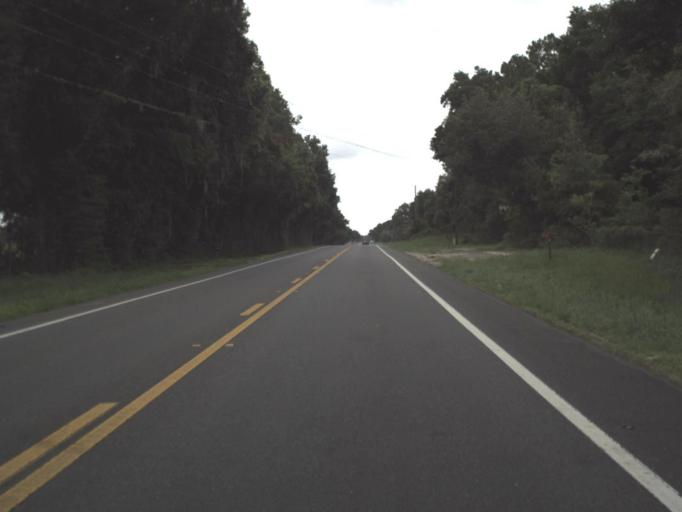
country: US
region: Florida
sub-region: Levy County
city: Williston
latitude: 29.3192
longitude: -82.4525
